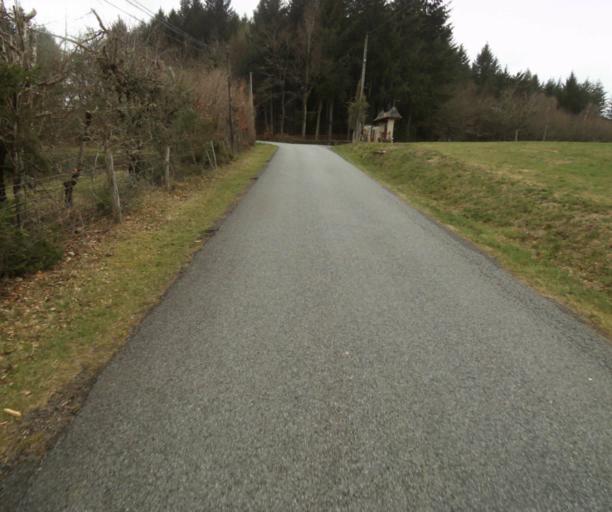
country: FR
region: Limousin
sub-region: Departement de la Correze
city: Correze
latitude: 45.3249
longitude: 1.9166
